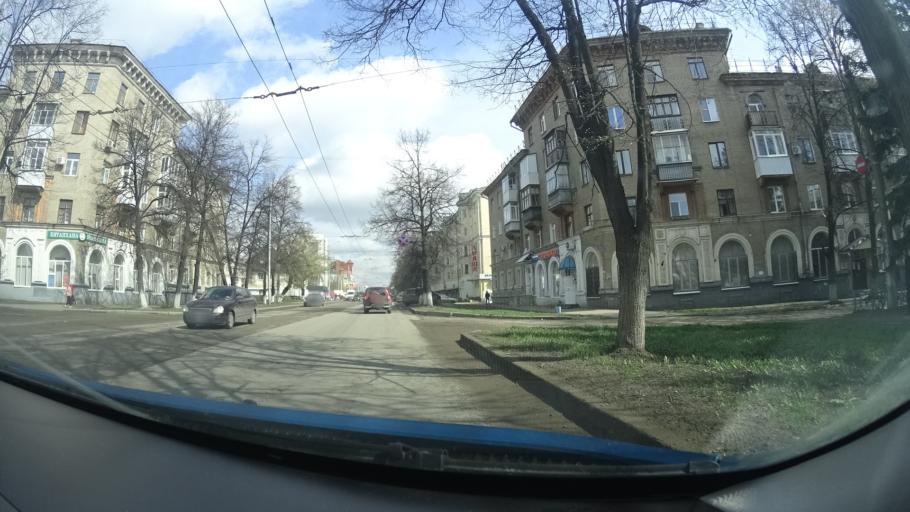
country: RU
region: Bashkortostan
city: Ufa
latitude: 54.8203
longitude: 56.0772
